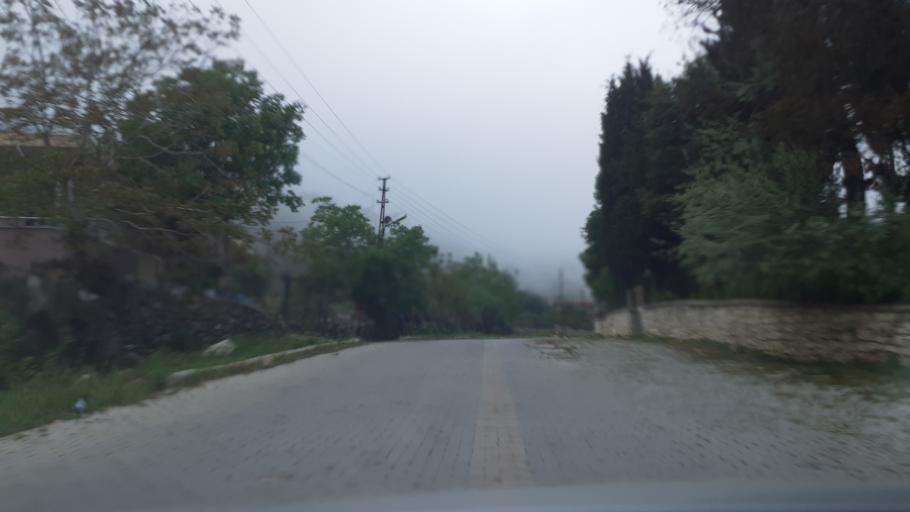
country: TR
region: Hatay
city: Yeditepe
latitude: 35.9676
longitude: 36.0116
